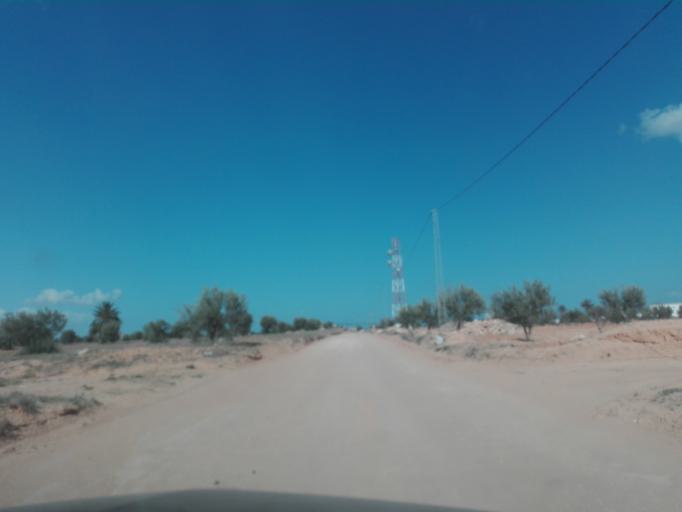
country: TN
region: Madanin
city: Bin Qirdan
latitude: 33.1666
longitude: 11.1964
